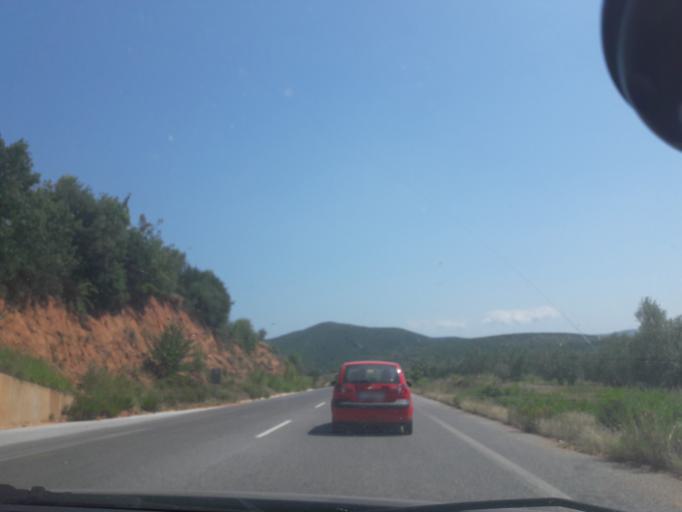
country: GR
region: Central Macedonia
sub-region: Nomos Chalkidikis
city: Megali Panagia
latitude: 40.3743
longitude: 23.6245
